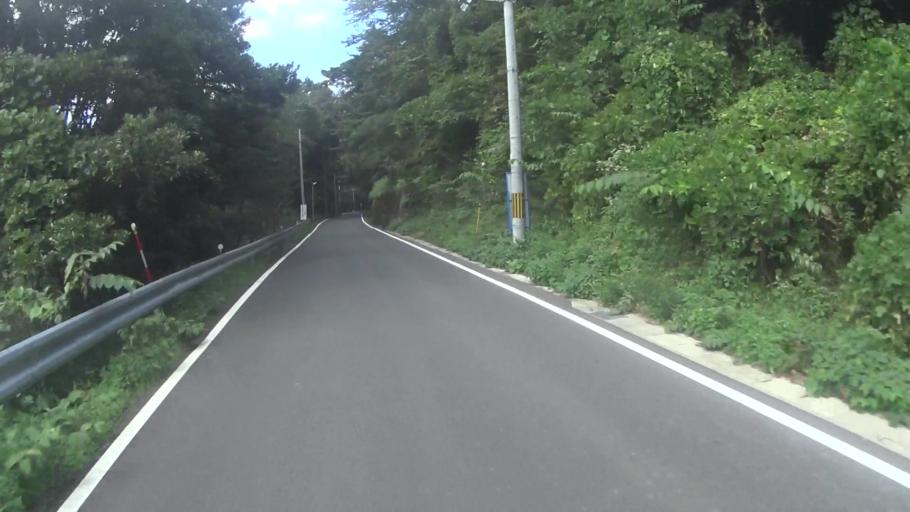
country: JP
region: Kyoto
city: Miyazu
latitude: 35.7428
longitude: 135.2447
